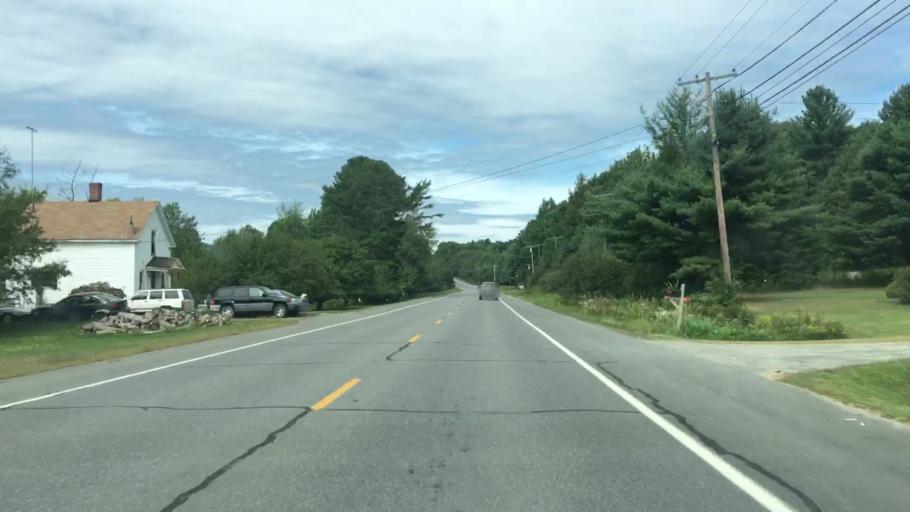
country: US
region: Maine
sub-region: Piscataquis County
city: Milo
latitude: 45.2738
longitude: -69.0014
